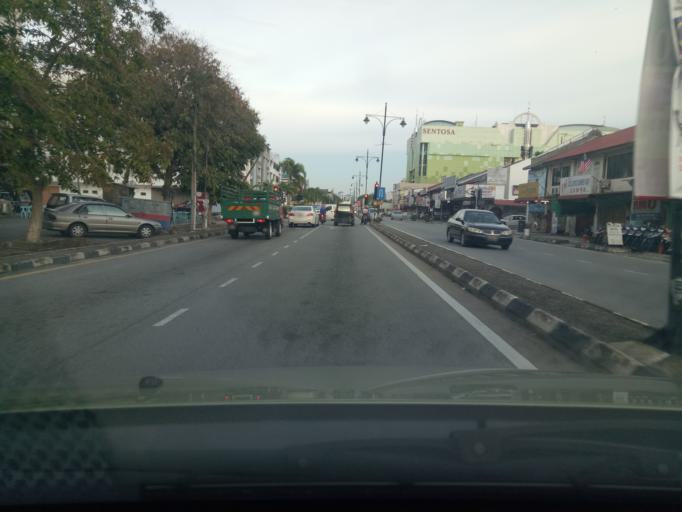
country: MY
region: Kedah
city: Alor Setar
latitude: 6.1233
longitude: 100.3620
